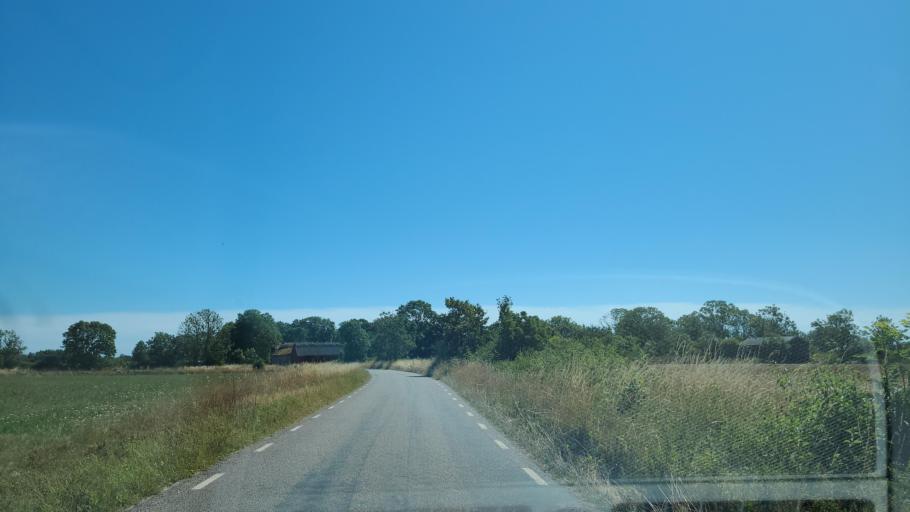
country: SE
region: Kalmar
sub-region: Borgholms Kommun
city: Borgholm
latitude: 56.7407
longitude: 16.7073
